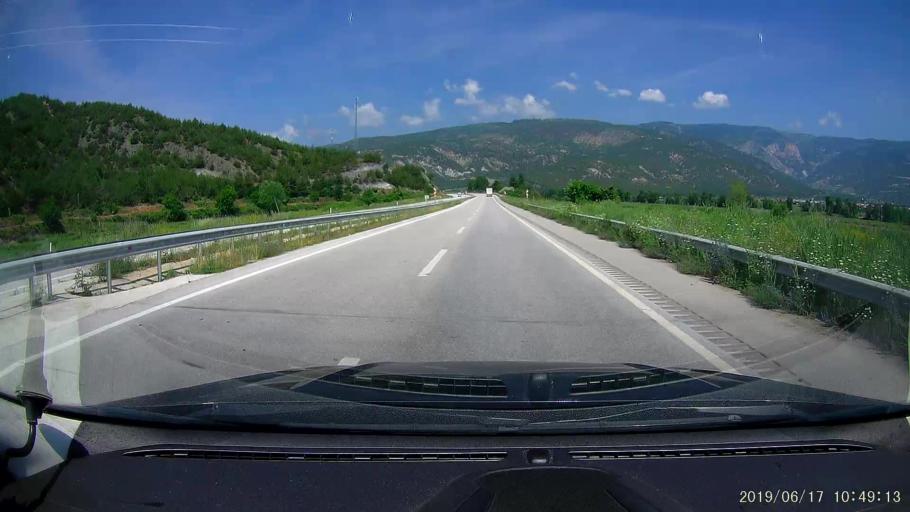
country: TR
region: Corum
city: Hacihamza
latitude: 41.0994
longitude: 34.4145
